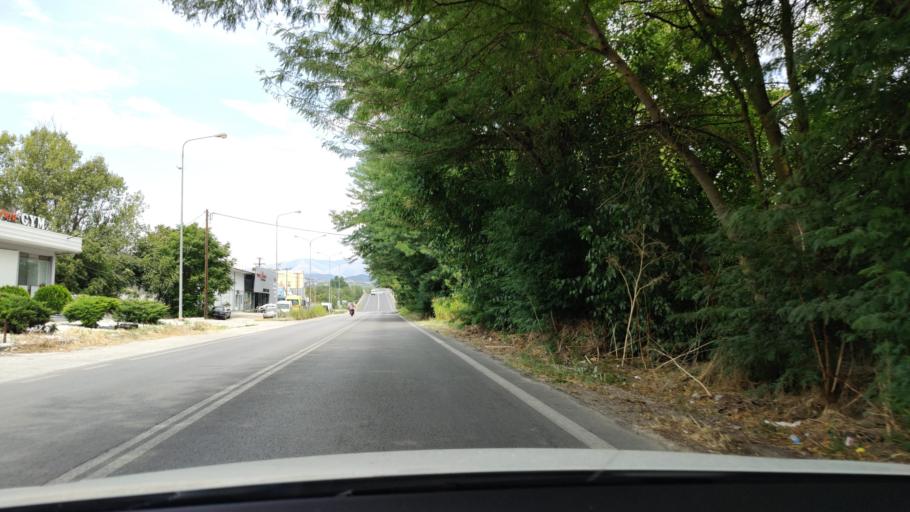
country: GR
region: Central Macedonia
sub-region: Nomos Serron
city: Serres
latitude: 41.0704
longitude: 23.5405
